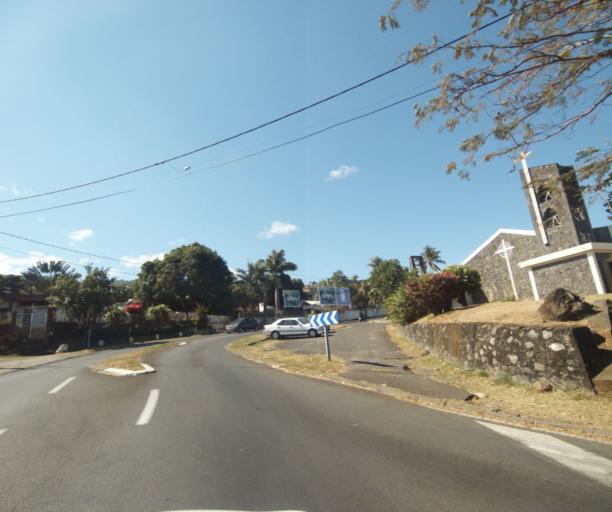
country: RE
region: Reunion
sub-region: Reunion
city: La Possession
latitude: -20.9825
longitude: 55.3343
